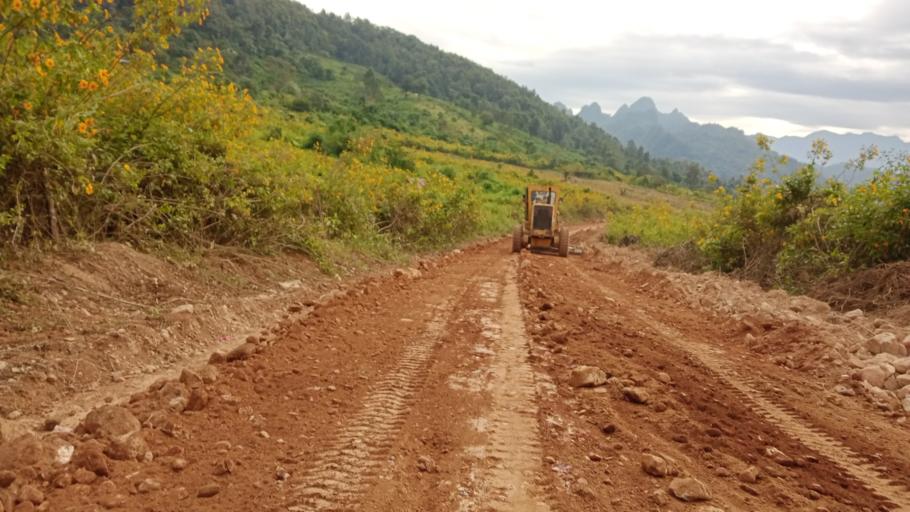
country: LA
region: Xiangkhoang
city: Phonsavan
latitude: 19.1169
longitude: 102.9222
